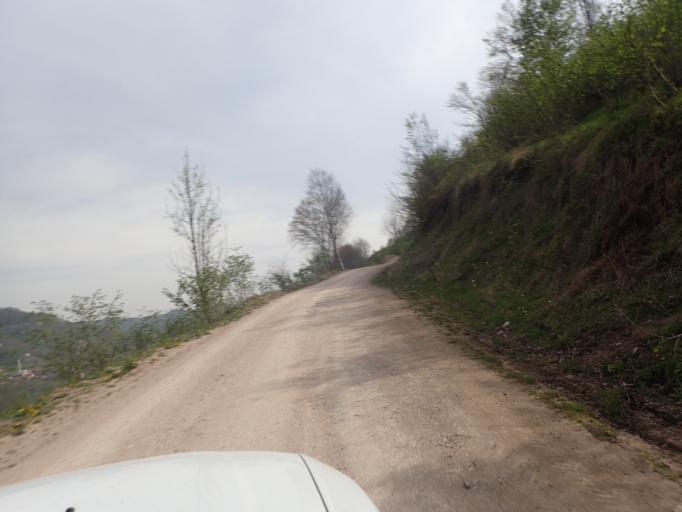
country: TR
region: Ordu
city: Aybasti
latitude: 40.7145
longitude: 37.2805
